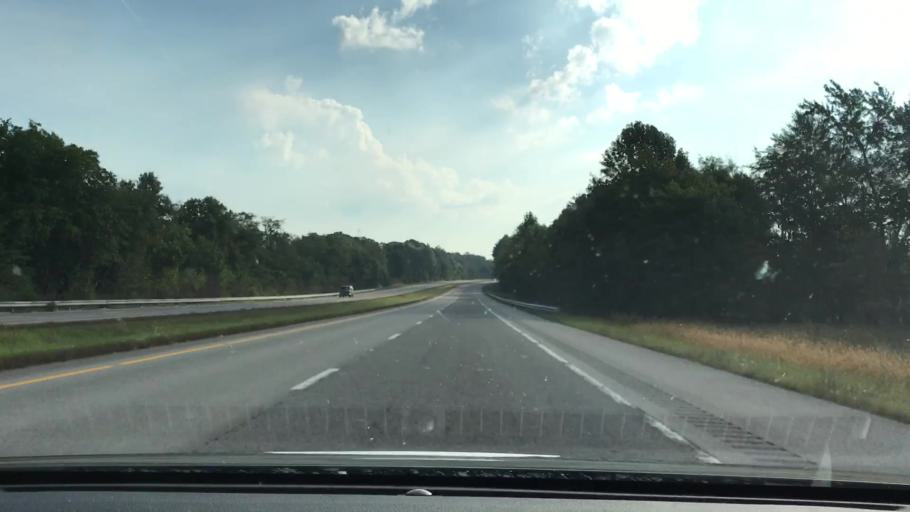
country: US
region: Kentucky
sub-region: Metcalfe County
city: Edmonton
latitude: 36.9981
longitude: -85.7301
